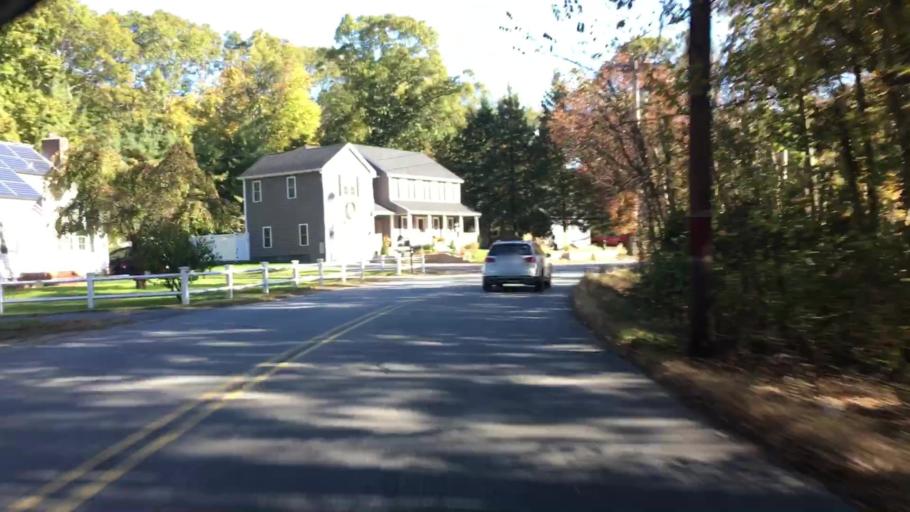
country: US
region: Massachusetts
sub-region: Middlesex County
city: Ashland
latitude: 42.2736
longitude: -71.4632
